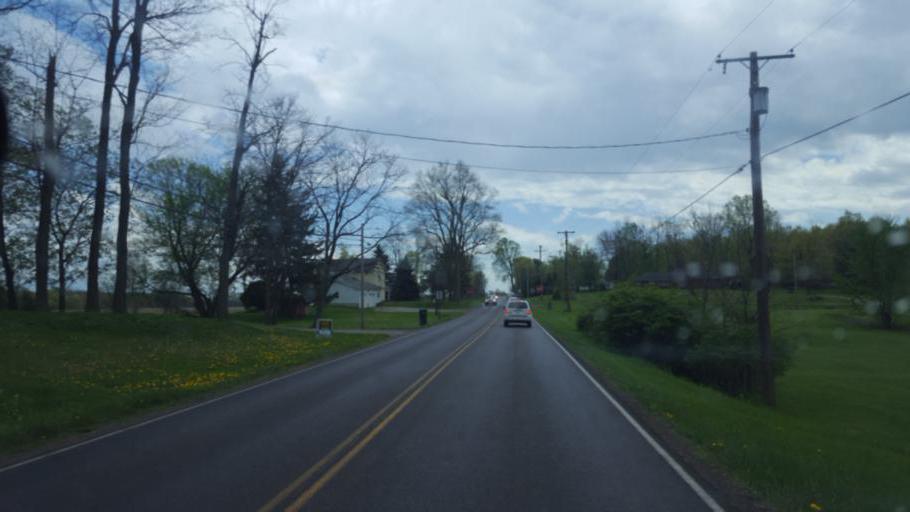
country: US
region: Ohio
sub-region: Richland County
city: Ontario
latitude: 40.7312
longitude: -82.5885
